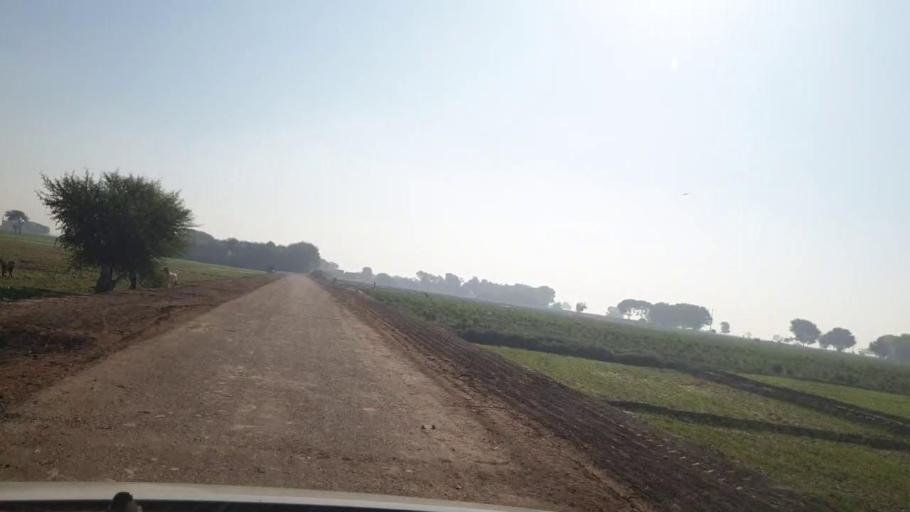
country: PK
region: Sindh
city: Dadu
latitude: 26.6383
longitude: 67.8324
